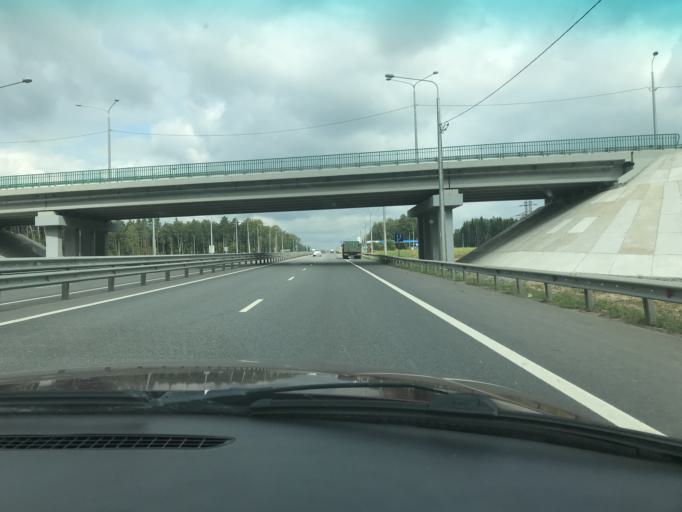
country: RU
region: Kaluga
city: Mstikhino
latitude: 54.6323
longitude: 36.1292
